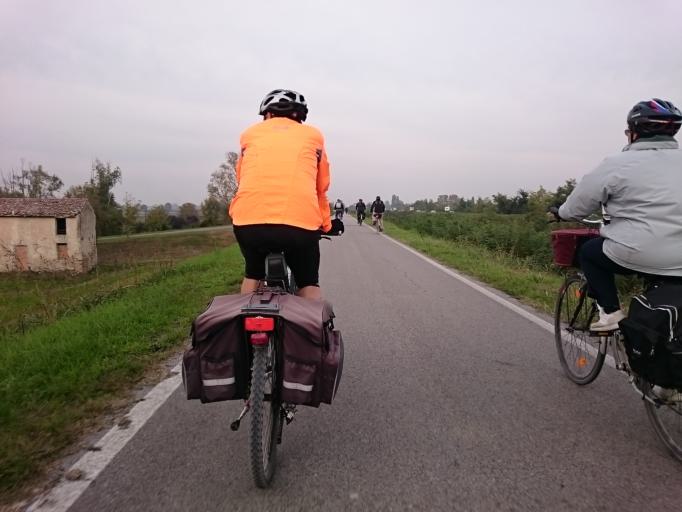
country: IT
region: Veneto
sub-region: Provincia di Padova
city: Battaglia Terme
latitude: 45.3054
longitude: 11.7959
